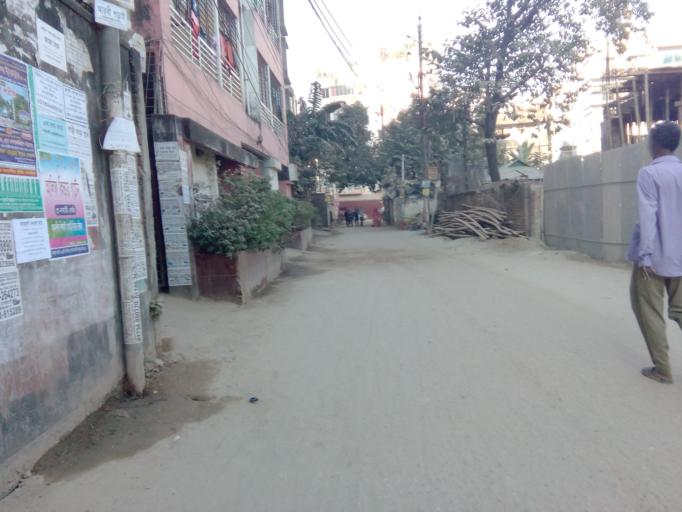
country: BD
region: Dhaka
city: Paltan
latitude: 23.7468
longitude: 90.4150
